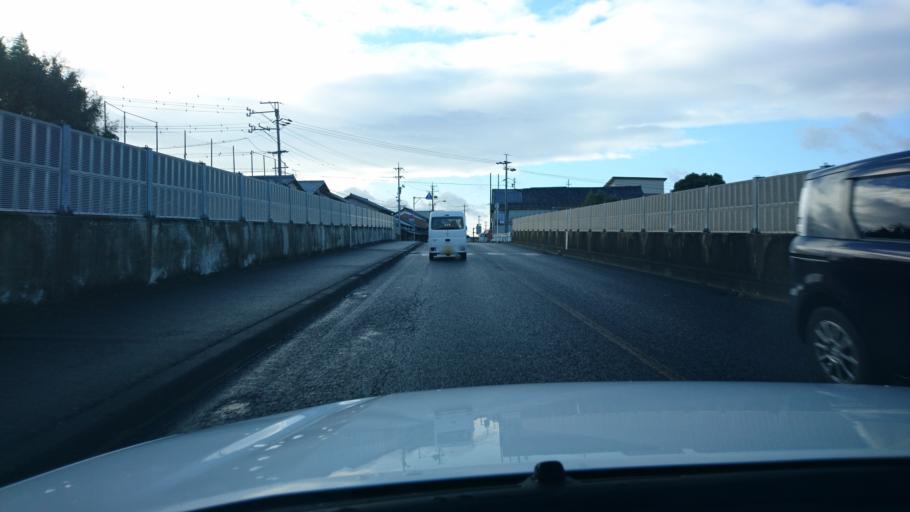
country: JP
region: Mie
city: Ueno-ebisumachi
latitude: 34.7706
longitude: 136.1236
